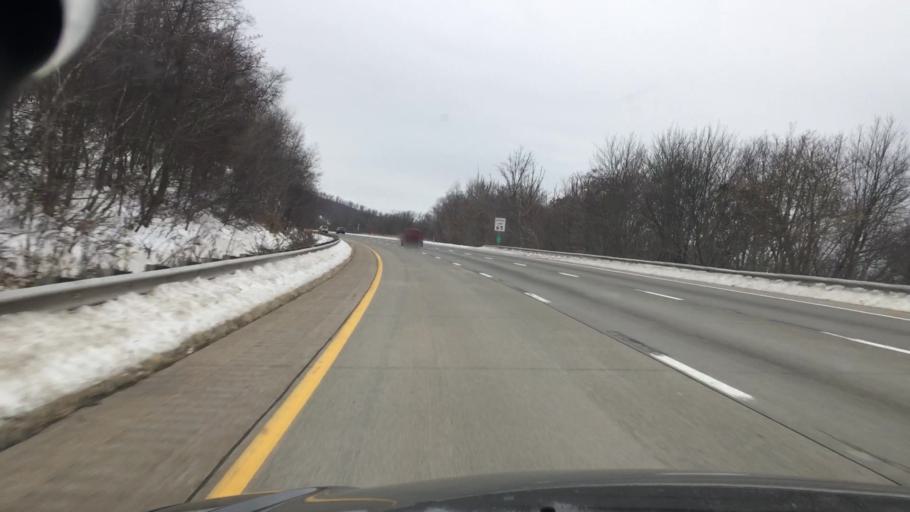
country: US
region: Pennsylvania
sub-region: Luzerne County
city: Harleigh
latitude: 41.0726
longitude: -75.9810
